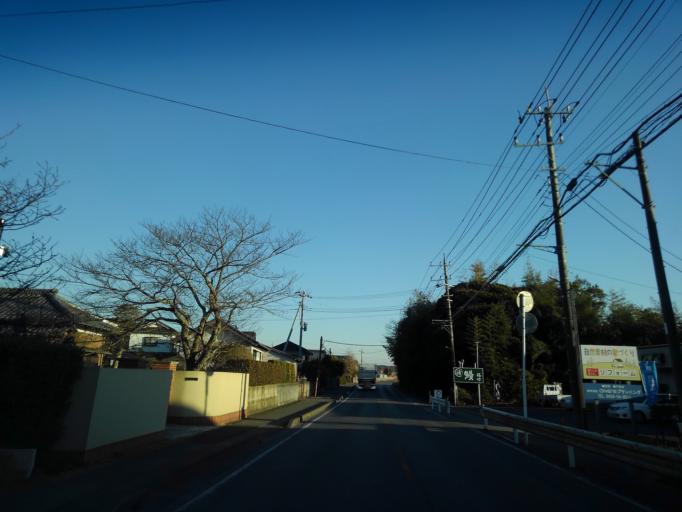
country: JP
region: Chiba
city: Kimitsu
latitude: 35.3172
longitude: 139.9303
